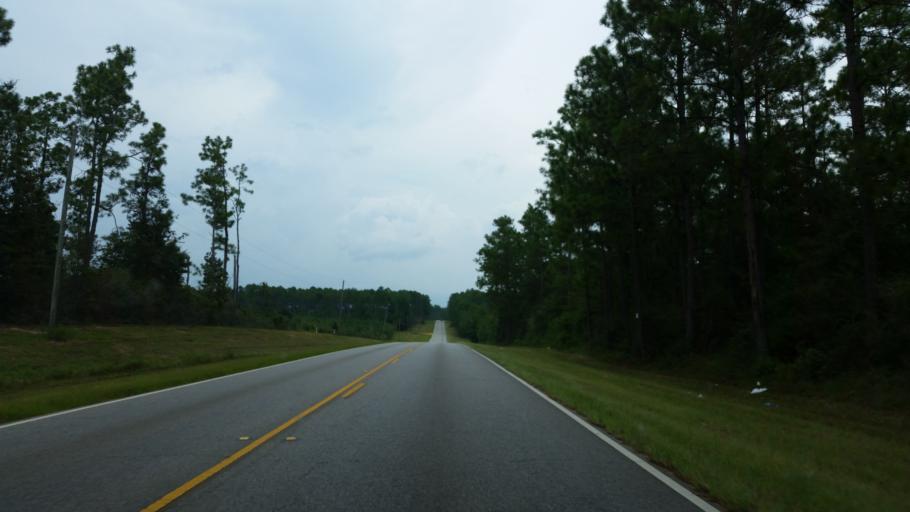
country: US
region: Florida
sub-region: Escambia County
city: Cantonment
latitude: 30.6569
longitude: -87.3090
